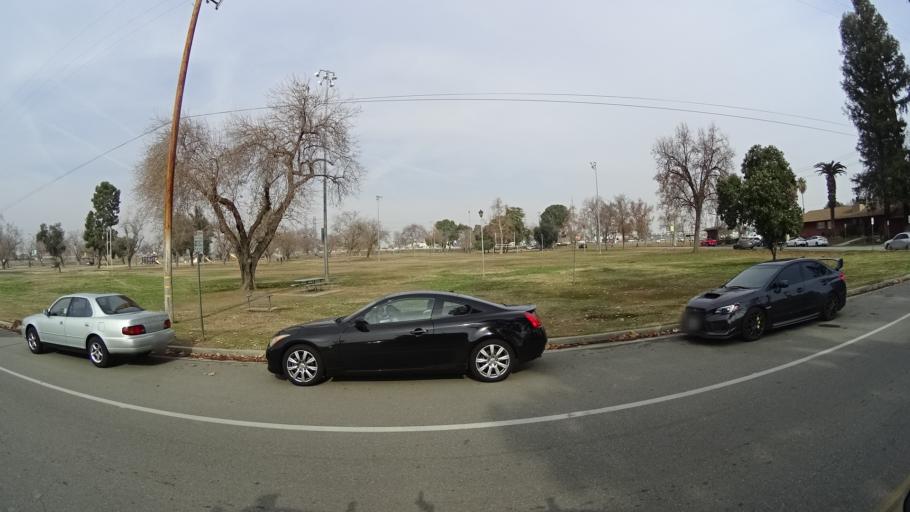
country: US
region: California
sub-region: Kern County
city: Bakersfield
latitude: 35.3781
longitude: -119.0395
